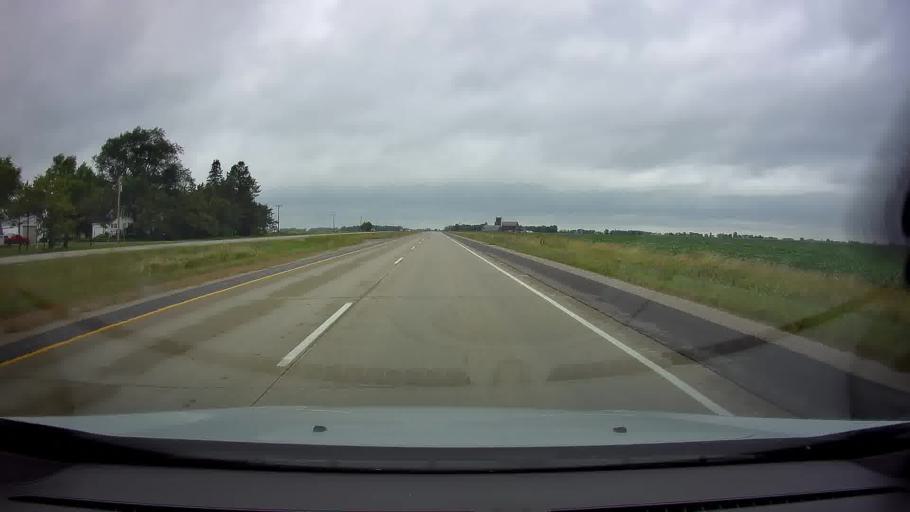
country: US
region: Wisconsin
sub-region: Brown County
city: Pulaski
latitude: 44.6044
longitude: -88.2513
